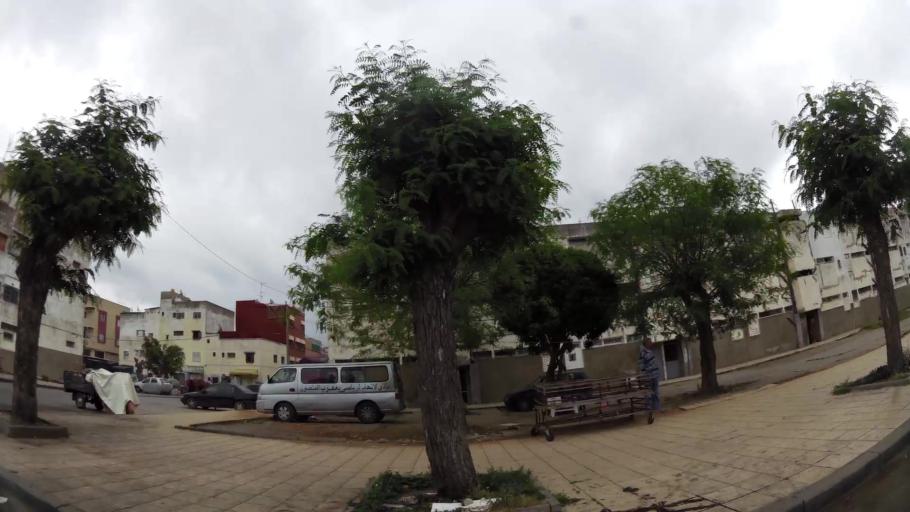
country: MA
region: Rabat-Sale-Zemmour-Zaer
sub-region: Rabat
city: Rabat
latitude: 33.9973
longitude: -6.8149
